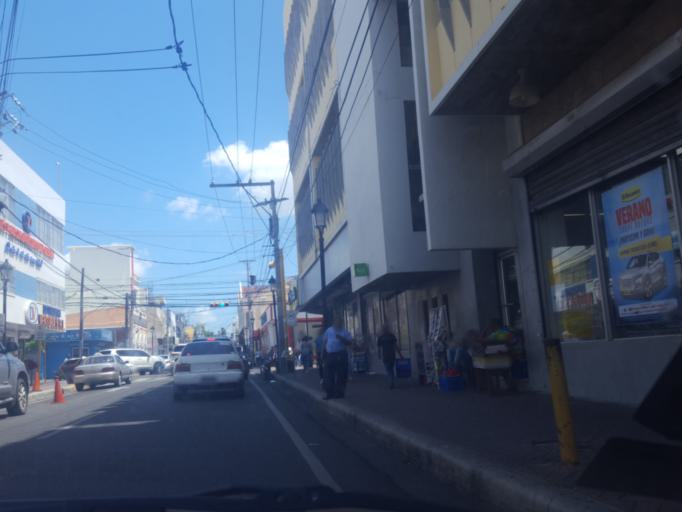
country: DO
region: Santiago
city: Santiago de los Caballeros
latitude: 19.4529
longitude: -70.7027
